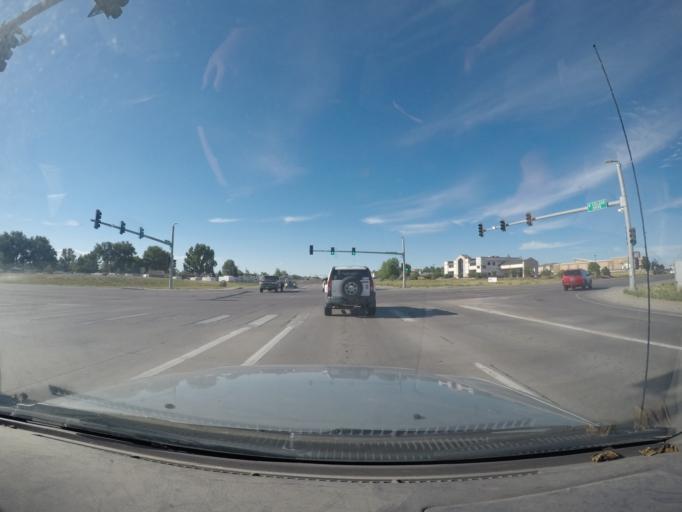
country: US
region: Wyoming
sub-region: Laramie County
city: Fox Farm-College
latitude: 41.1414
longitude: -104.7613
